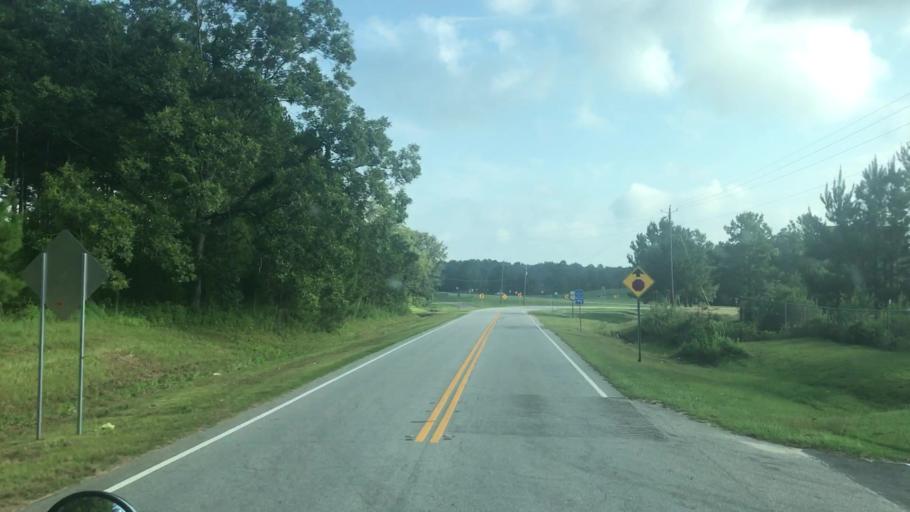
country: US
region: Georgia
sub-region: Decatur County
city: Bainbridge
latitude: 30.7740
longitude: -84.4886
